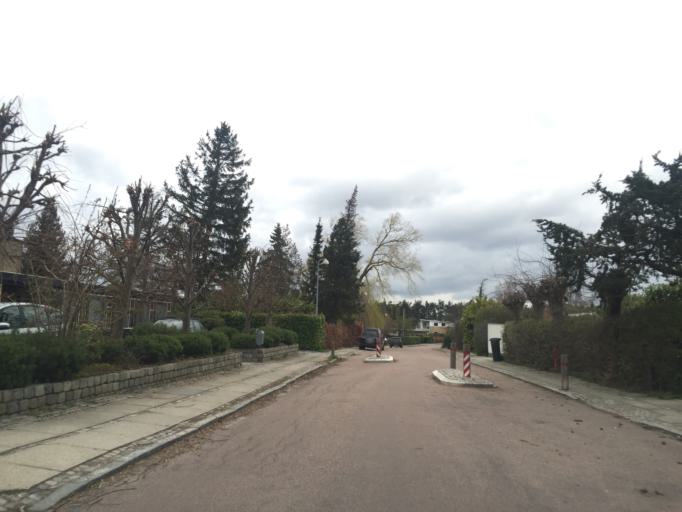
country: DK
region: Capital Region
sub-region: Rudersdal Kommune
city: Holte
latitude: 55.7881
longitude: 12.4475
